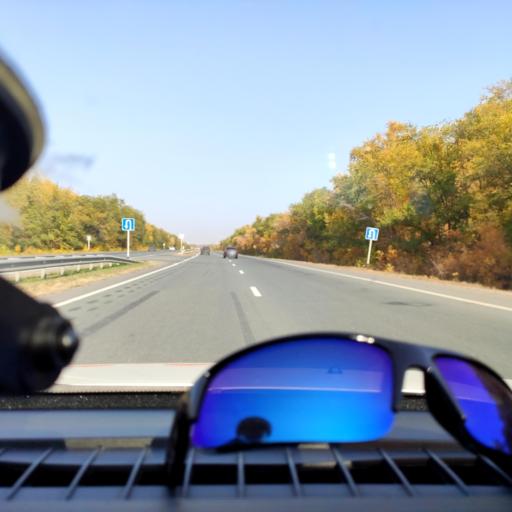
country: RU
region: Samara
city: Novokuybyshevsk
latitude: 53.0295
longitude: 49.9940
